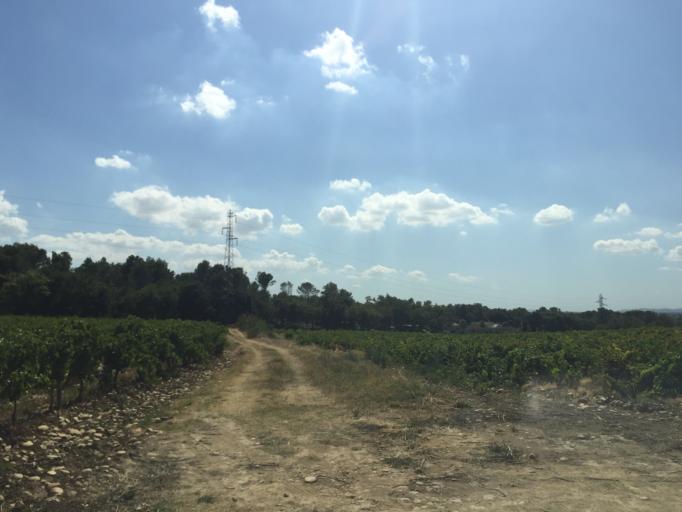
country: FR
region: Provence-Alpes-Cote d'Azur
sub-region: Departement du Vaucluse
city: Bedarrides
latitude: 44.0235
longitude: 4.8928
